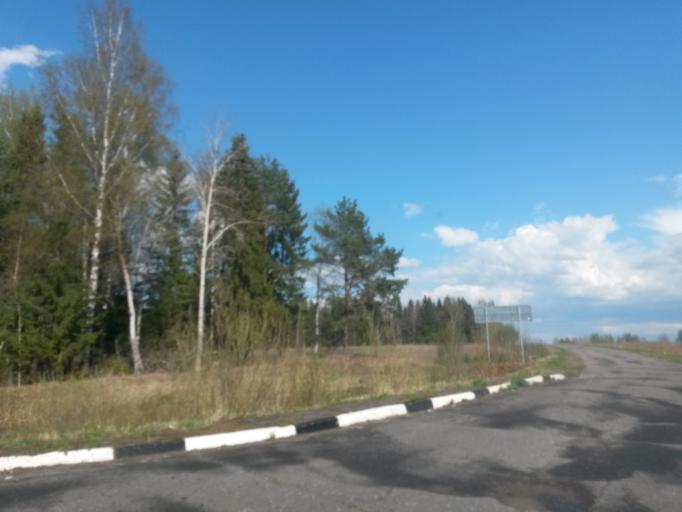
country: RU
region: Jaroslavl
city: Tutayev
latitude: 57.9716
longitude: 39.5085
